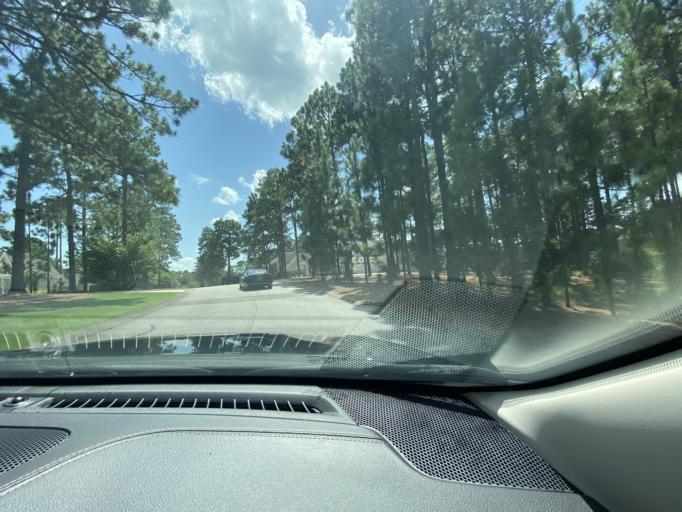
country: US
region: North Carolina
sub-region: Moore County
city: Pinehurst
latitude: 35.1949
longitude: -79.4309
